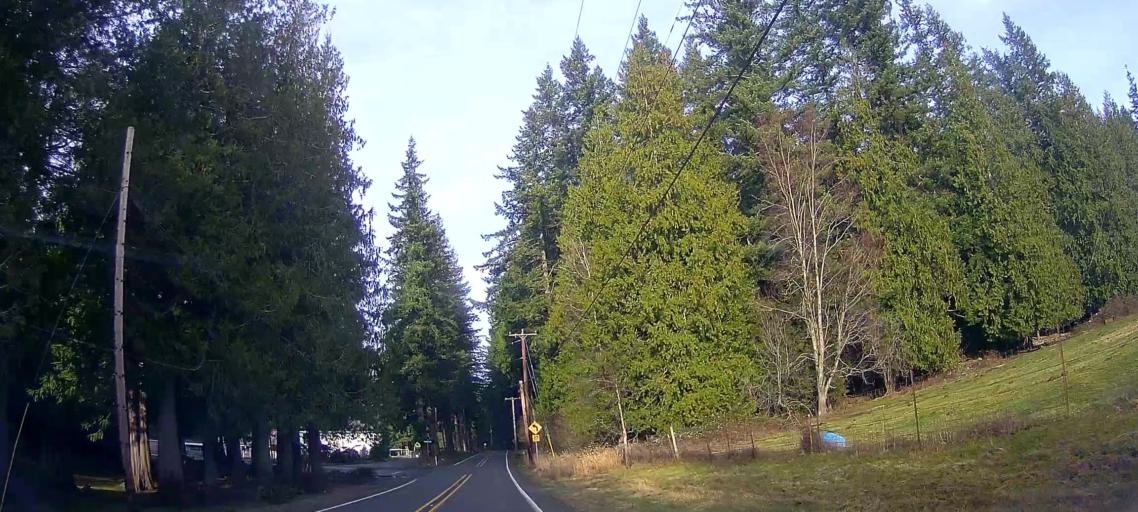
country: US
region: Washington
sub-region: Skagit County
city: Sedro-Woolley
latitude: 48.5847
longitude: -122.2242
